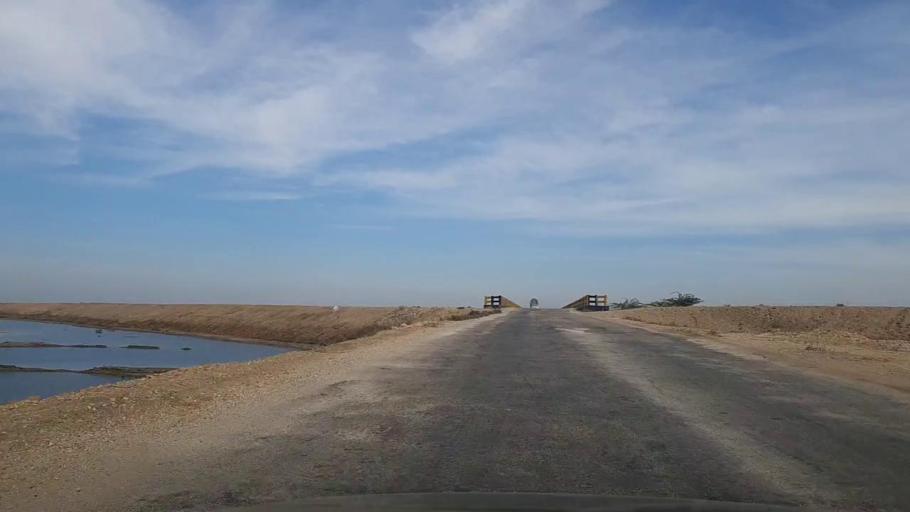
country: PK
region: Sindh
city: Daro Mehar
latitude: 24.9031
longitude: 68.0682
